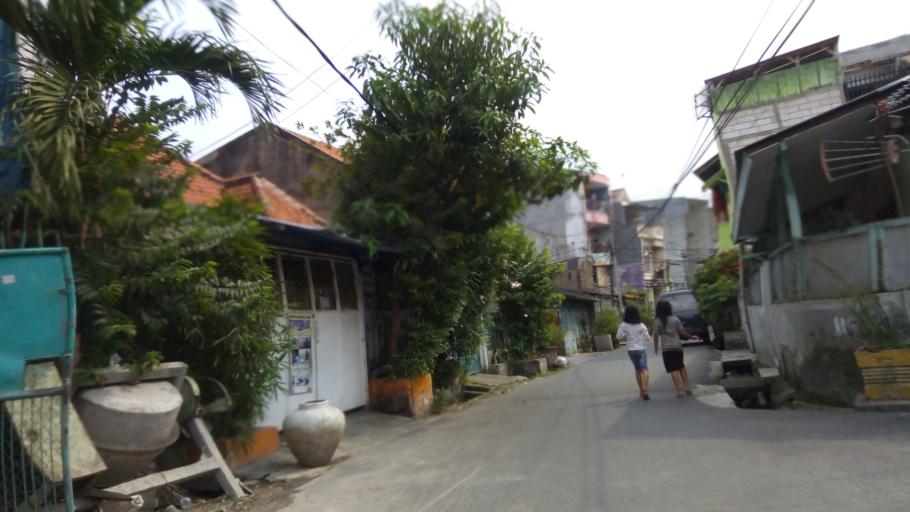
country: ID
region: Jakarta Raya
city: Jakarta
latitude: -6.1559
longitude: 106.8337
